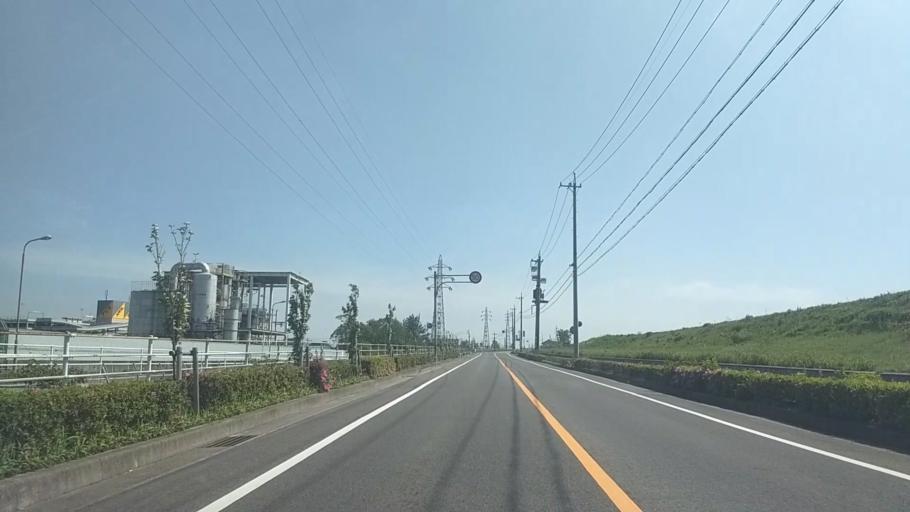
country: JP
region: Aichi
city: Okazaki
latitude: 34.9786
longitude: 137.1503
